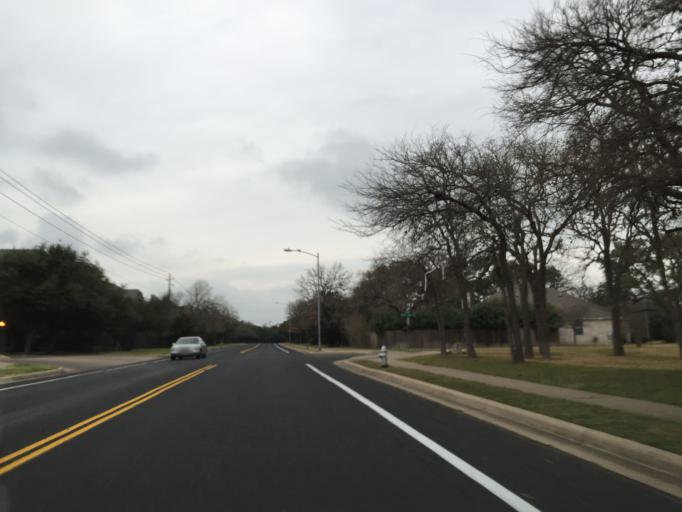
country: US
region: Texas
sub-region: Travis County
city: Barton Creek
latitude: 30.2465
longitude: -97.8396
